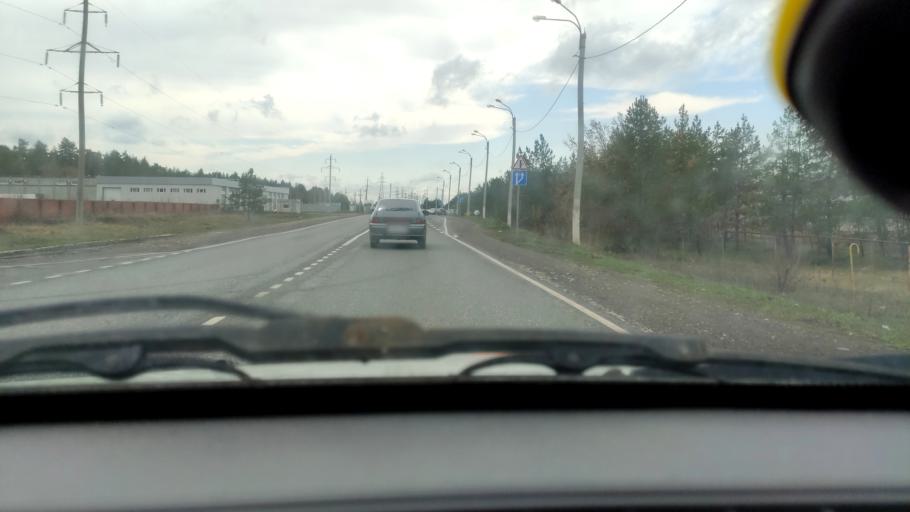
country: RU
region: Samara
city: Zhigulevsk
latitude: 53.5686
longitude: 49.5494
